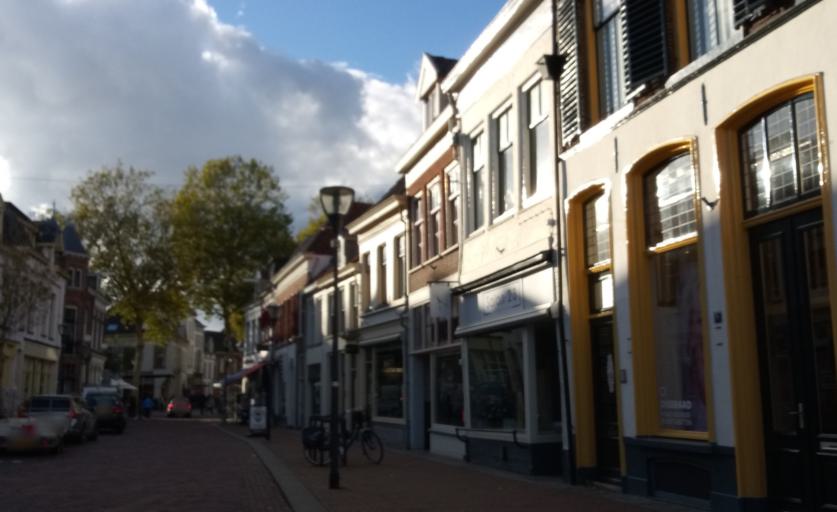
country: NL
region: Gelderland
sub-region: Gemeente Zutphen
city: Zutphen
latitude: 52.1412
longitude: 6.2007
